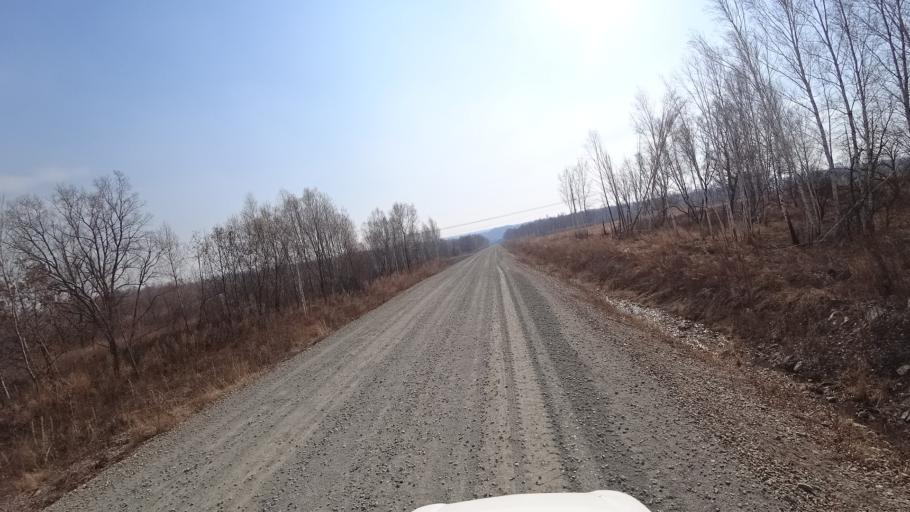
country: RU
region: Amur
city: Novobureyskiy
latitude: 49.8043
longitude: 129.9630
